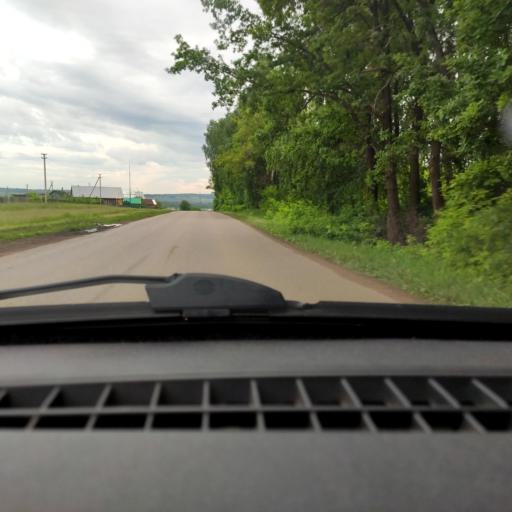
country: RU
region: Bashkortostan
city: Chishmy
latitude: 54.5992
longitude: 55.4436
